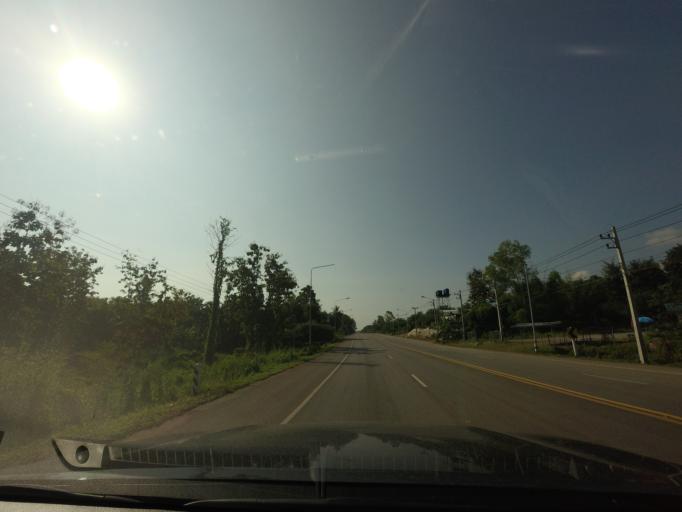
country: TH
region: Phetchabun
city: Lom Kao
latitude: 16.8645
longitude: 101.1712
